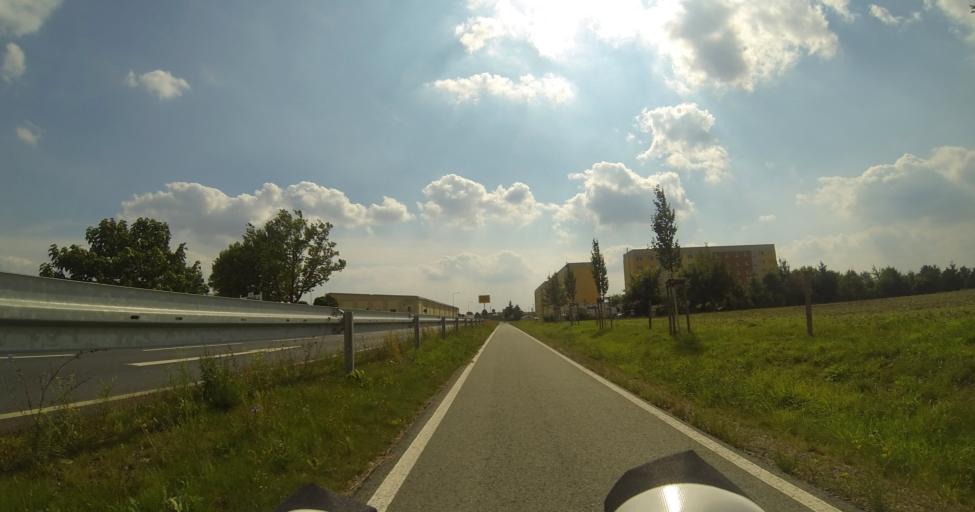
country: DE
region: Saxony
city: Grossenhain
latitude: 51.3053
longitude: 13.5364
